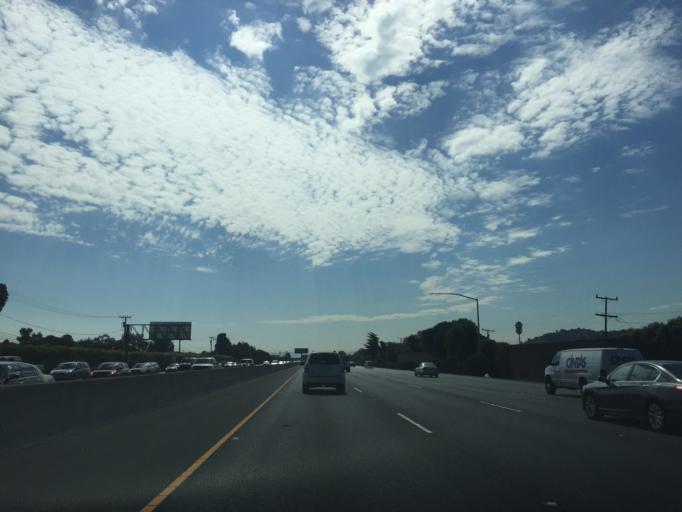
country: US
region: California
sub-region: San Mateo County
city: Belmont
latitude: 37.5403
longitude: -122.2841
